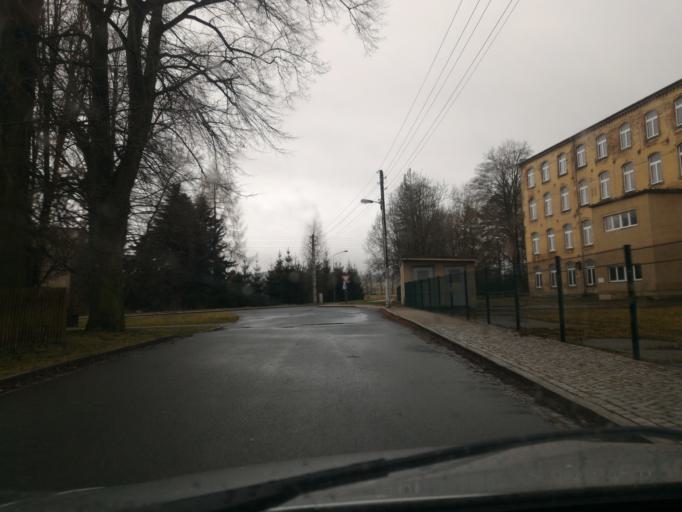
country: DE
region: Saxony
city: Seifhennersdorf
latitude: 50.9317
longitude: 14.6094
